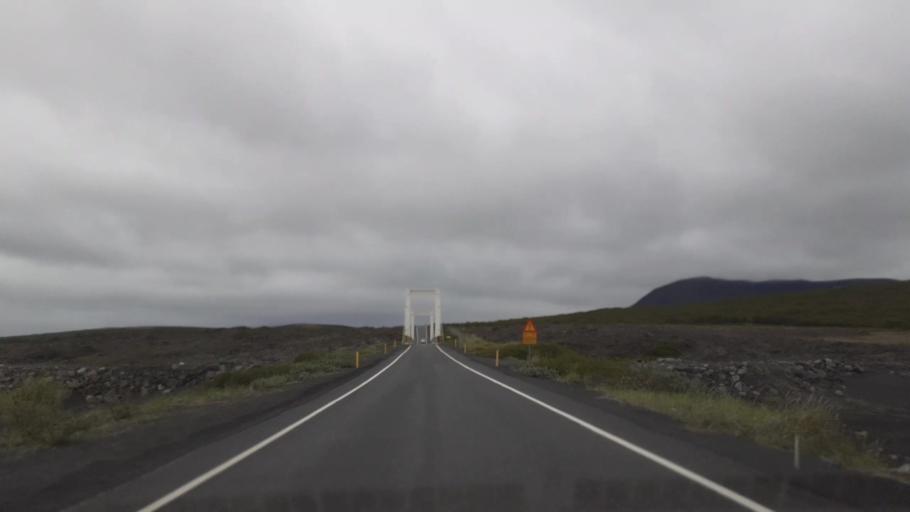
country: IS
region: Northeast
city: Husavik
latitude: 66.0318
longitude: -16.4463
